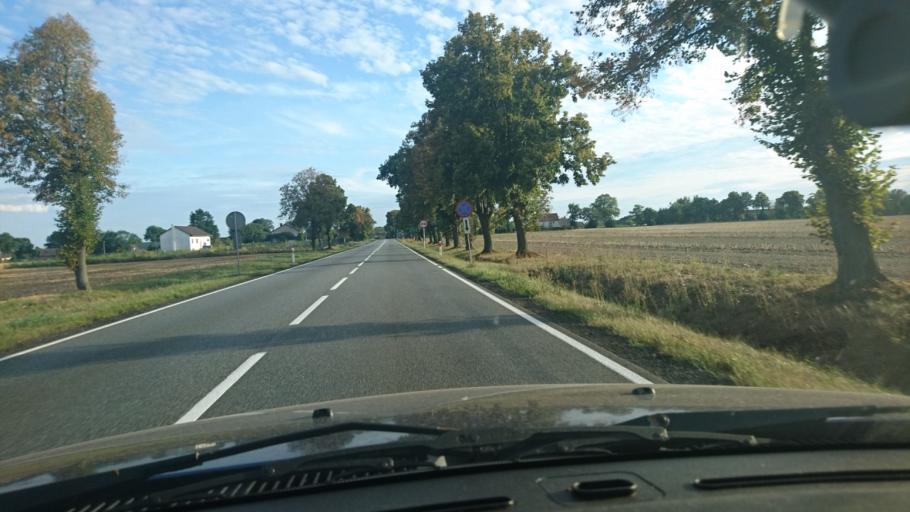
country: PL
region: Opole Voivodeship
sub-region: Powiat kluczborski
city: Kluczbork
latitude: 51.0327
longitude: 18.1929
